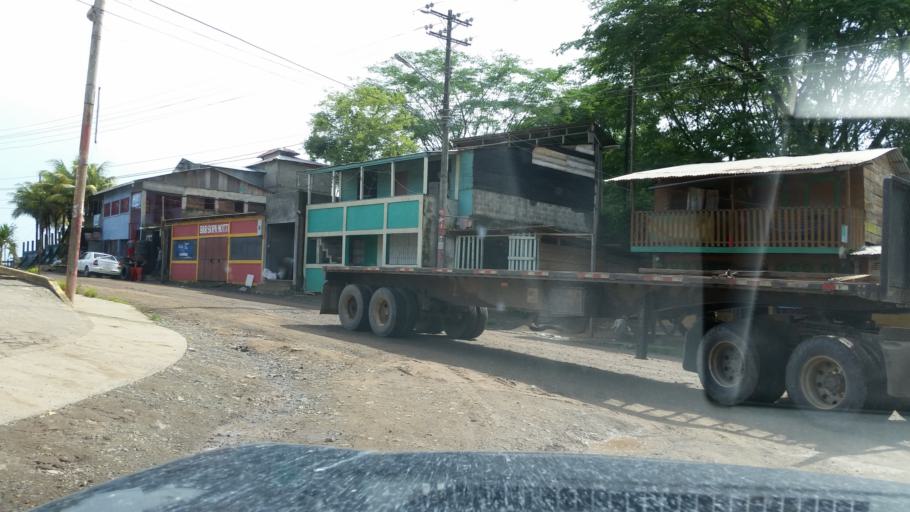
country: NI
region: Atlantico Norte (RAAN)
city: Siuna
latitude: 13.7162
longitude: -84.7724
